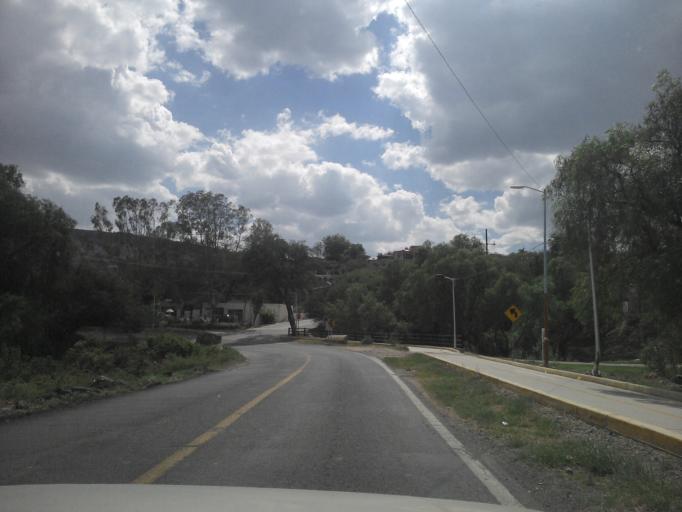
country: MX
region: Guanajuato
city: San Francisco del Rincon
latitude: 21.0312
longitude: -101.8869
